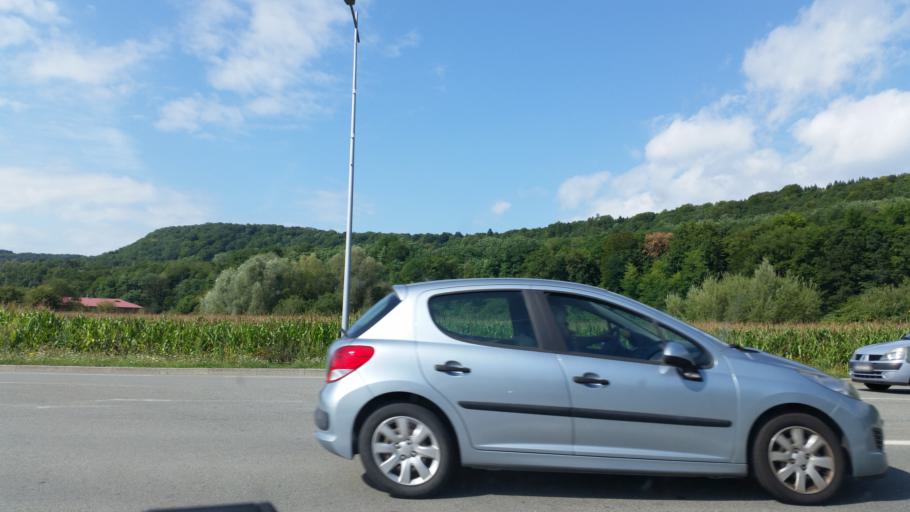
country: FR
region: Franche-Comte
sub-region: Departement du Doubs
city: Mathay
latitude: 47.4416
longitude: 6.7777
